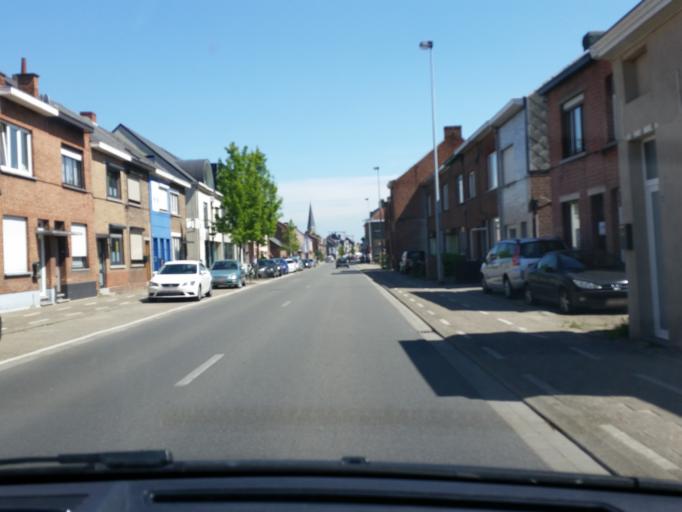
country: BE
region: Flanders
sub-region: Provincie Antwerpen
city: Bonheiden
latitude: 51.0248
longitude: 4.5404
